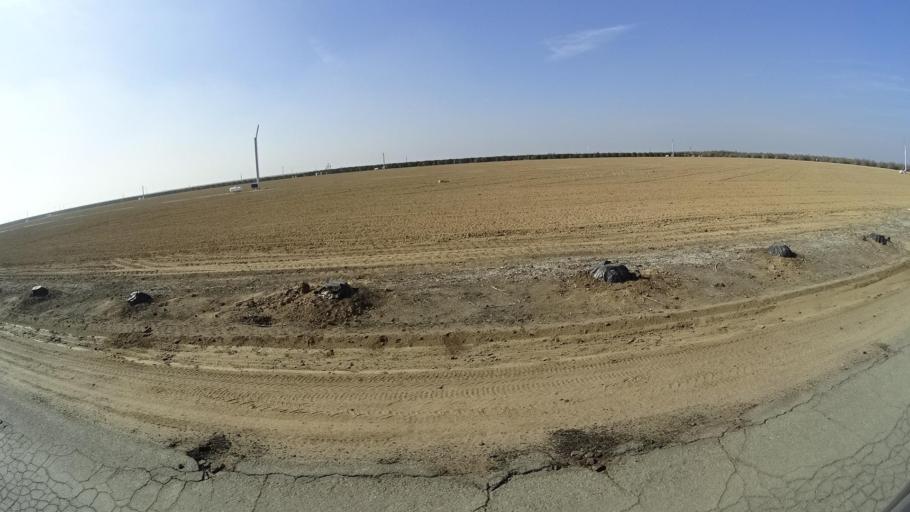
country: US
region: California
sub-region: Kern County
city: Shafter
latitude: 35.5419
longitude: -119.1335
